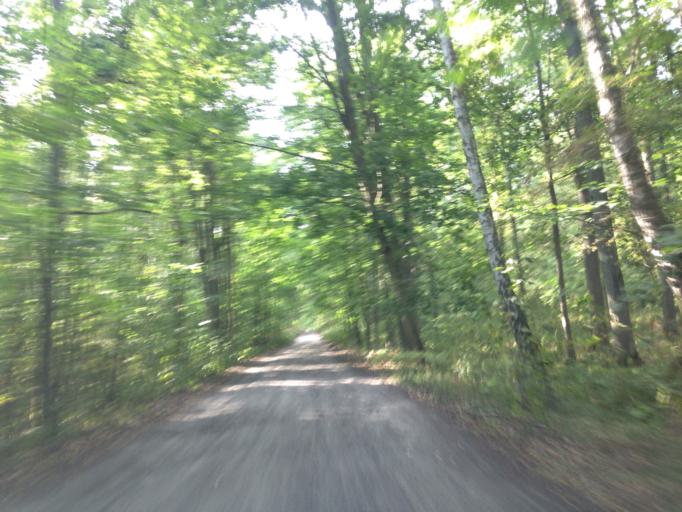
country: PL
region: Kujawsko-Pomorskie
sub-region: Powiat swiecki
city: Swiekatowo
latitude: 53.4977
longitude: 18.1184
